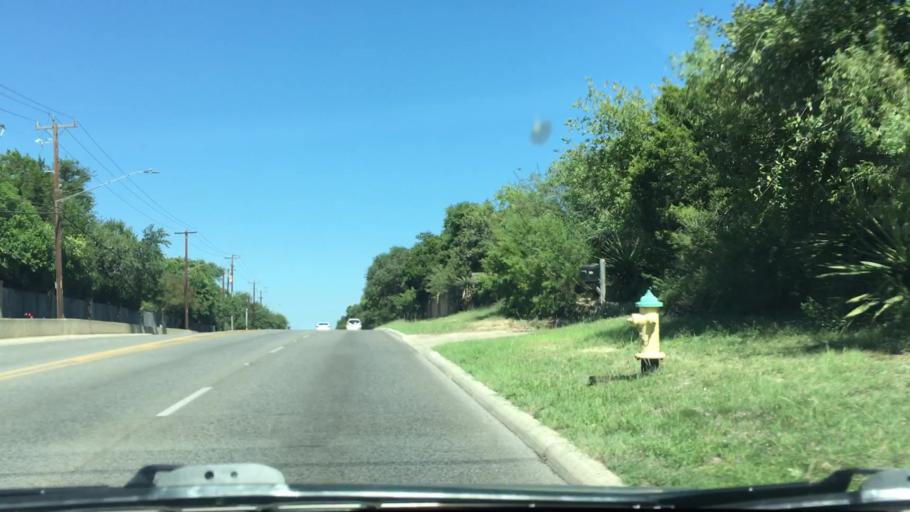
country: US
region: Texas
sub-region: Bexar County
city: Hollywood Park
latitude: 29.5738
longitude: -98.4937
